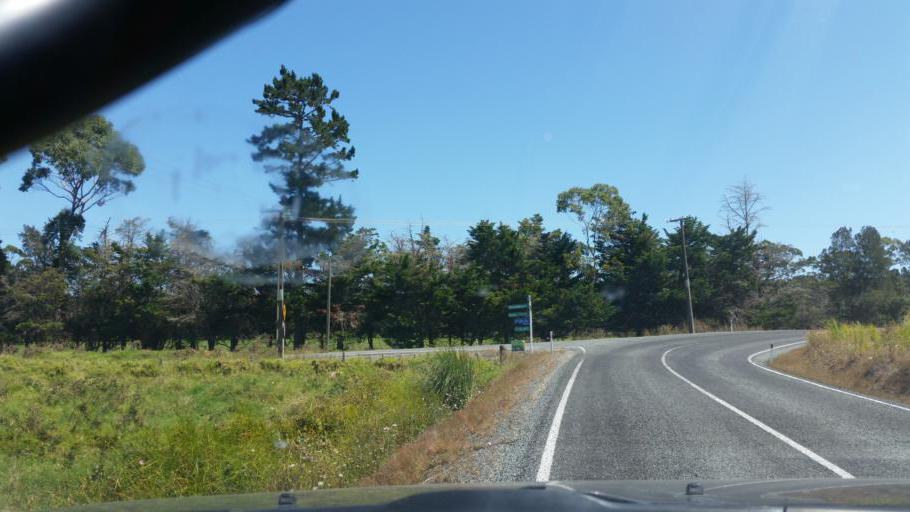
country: NZ
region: Northland
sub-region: Kaipara District
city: Dargaville
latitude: -36.0077
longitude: 173.9589
